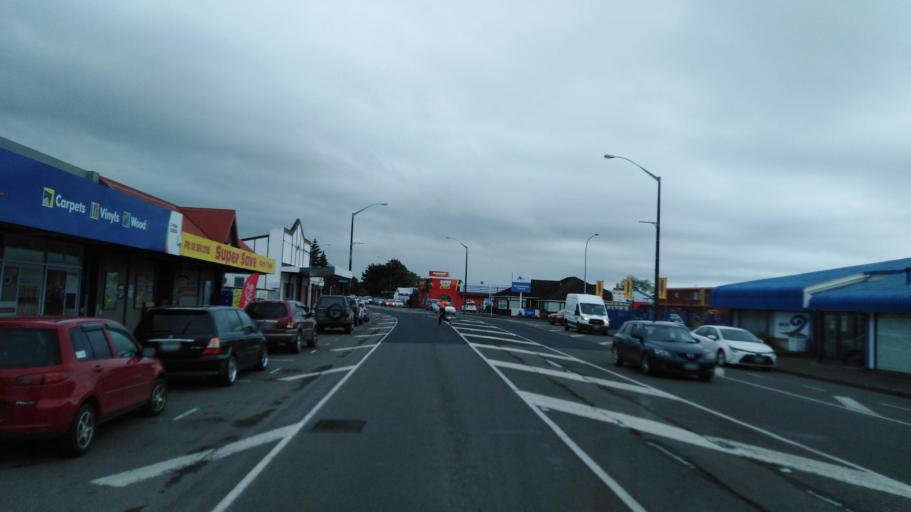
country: NZ
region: Manawatu-Wanganui
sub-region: Horowhenua District
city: Levin
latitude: -40.6268
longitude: 175.2816
